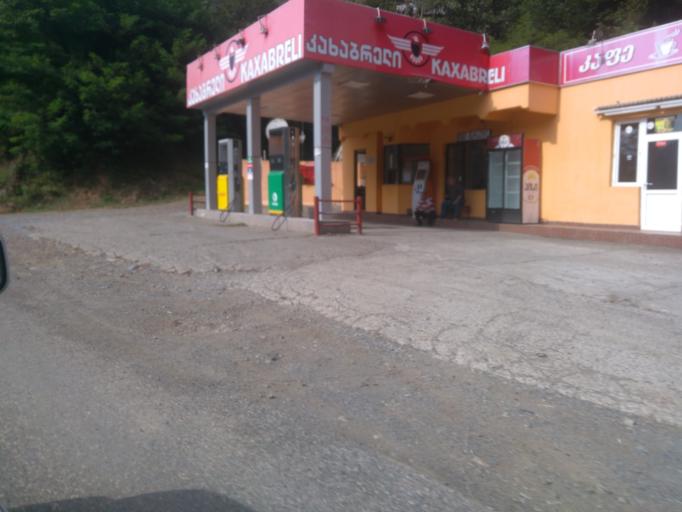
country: TR
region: Artvin
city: Muratli
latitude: 41.5462
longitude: 41.7817
